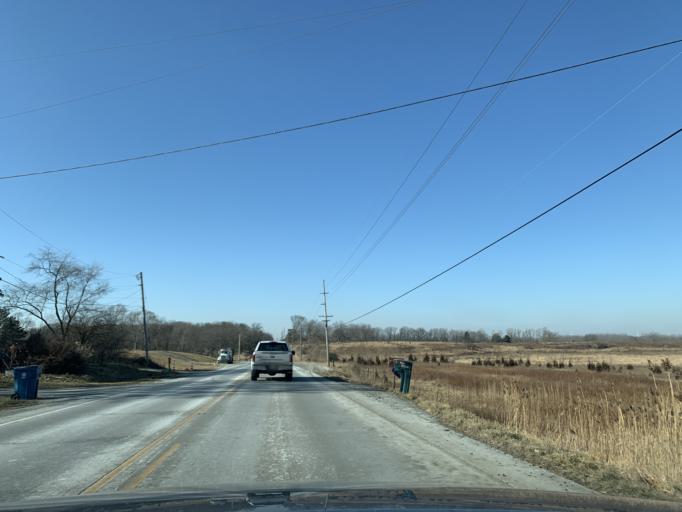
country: US
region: Indiana
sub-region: Lake County
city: Crown Point
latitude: 41.4207
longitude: -87.4019
